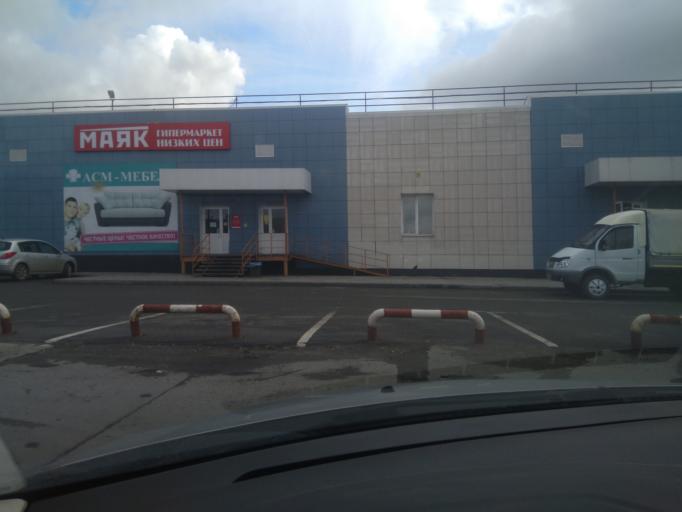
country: RU
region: Sverdlovsk
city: Nizhniy Tagil
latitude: 57.9078
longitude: 60.0234
